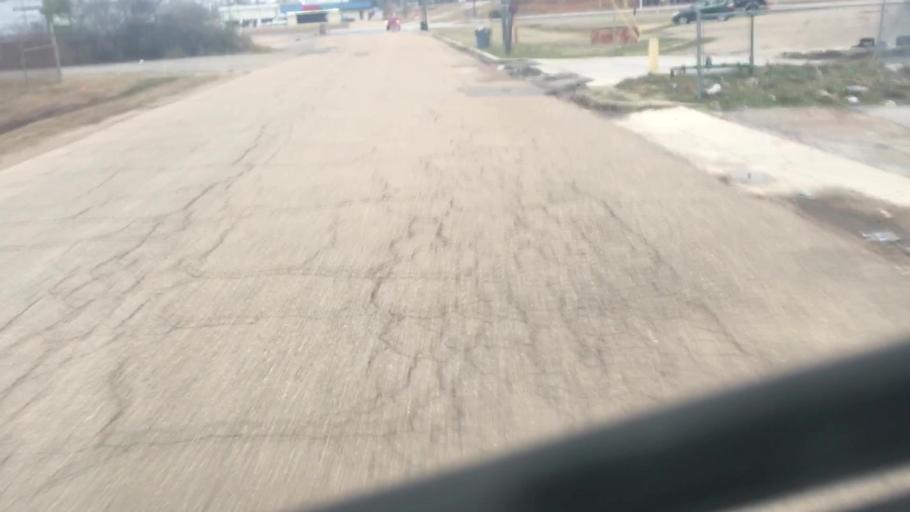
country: US
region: Alabama
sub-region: Walker County
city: Jasper
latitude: 33.8350
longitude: -87.2254
